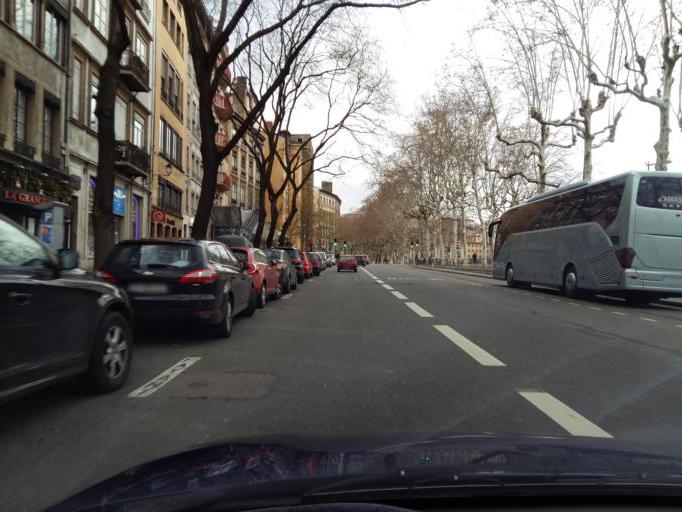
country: FR
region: Rhone-Alpes
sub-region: Departement du Rhone
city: Lyon
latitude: 45.7635
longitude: 4.8290
